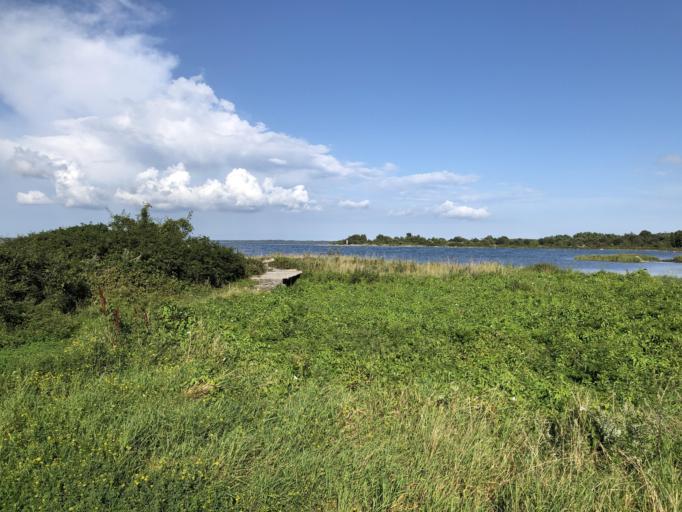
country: SE
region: Gotland
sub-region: Gotland
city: Hemse
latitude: 56.9956
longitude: 18.1981
